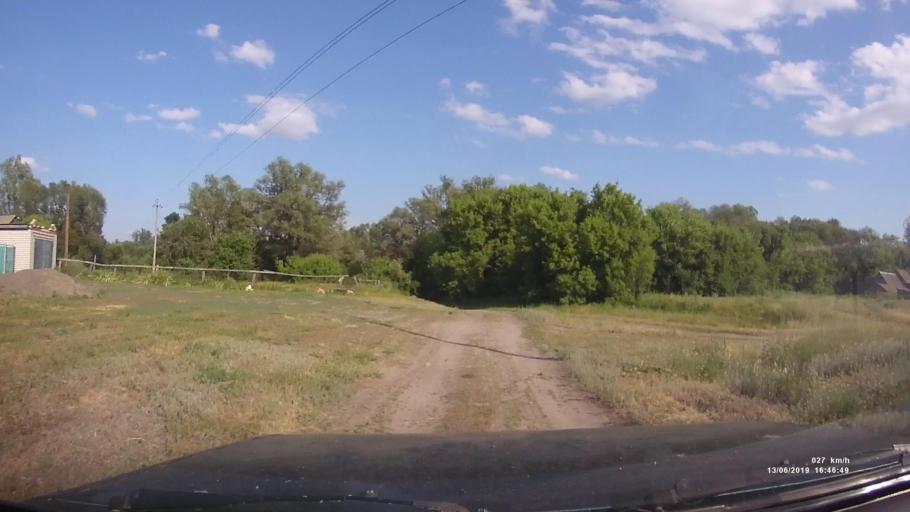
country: RU
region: Rostov
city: Kazanskaya
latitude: 49.9446
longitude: 41.4292
